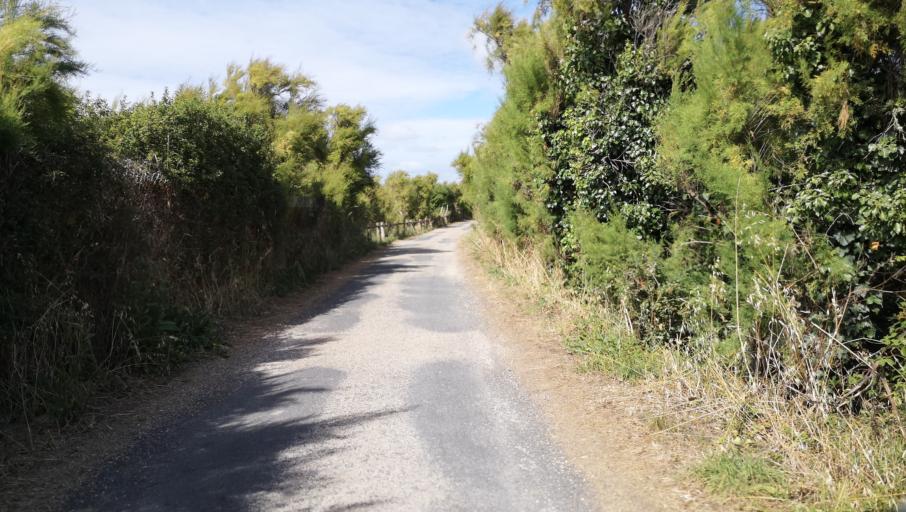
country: FR
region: Pays de la Loire
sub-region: Departement de la Vendee
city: Olonne-sur-Mer
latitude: 46.5392
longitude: -1.8033
